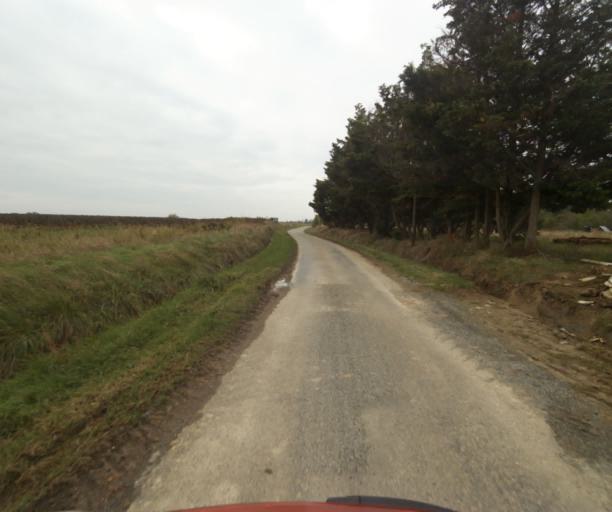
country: FR
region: Midi-Pyrenees
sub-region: Departement du Tarn-et-Garonne
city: Verdun-sur-Garonne
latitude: 43.8123
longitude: 1.1927
